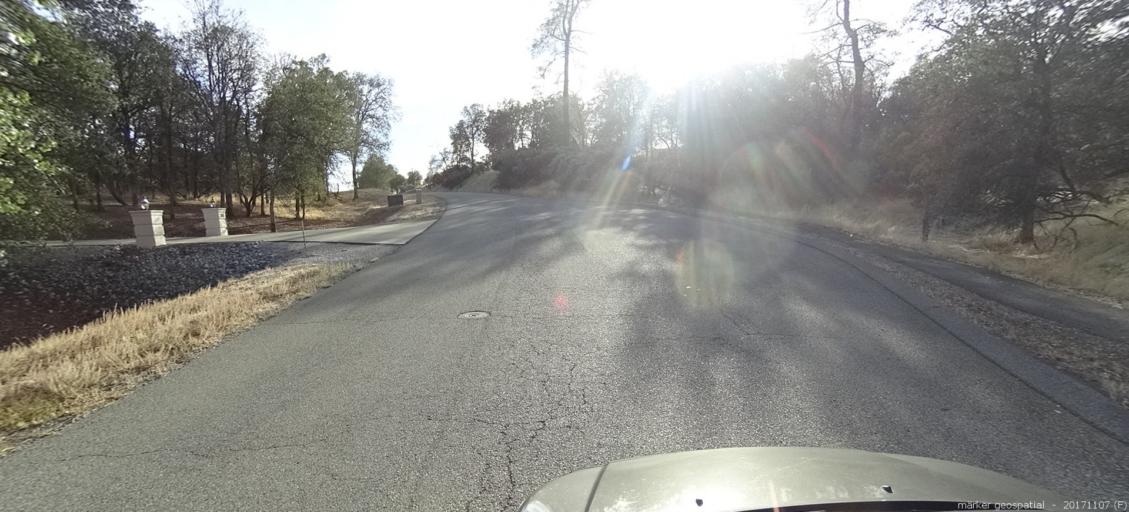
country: US
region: California
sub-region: Shasta County
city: Shasta
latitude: 40.5126
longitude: -122.4734
